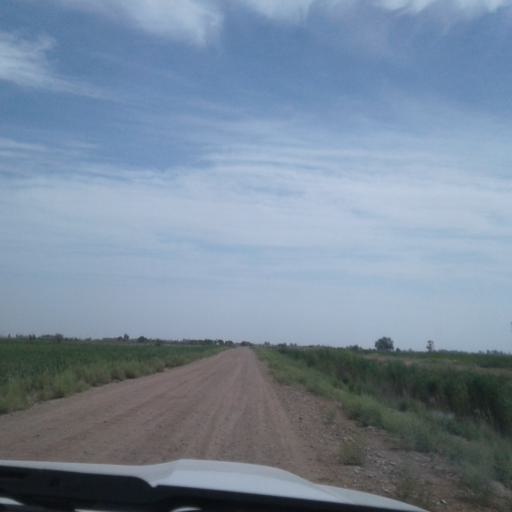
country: TM
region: Dasoguz
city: Tagta
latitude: 41.5433
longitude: 59.8093
